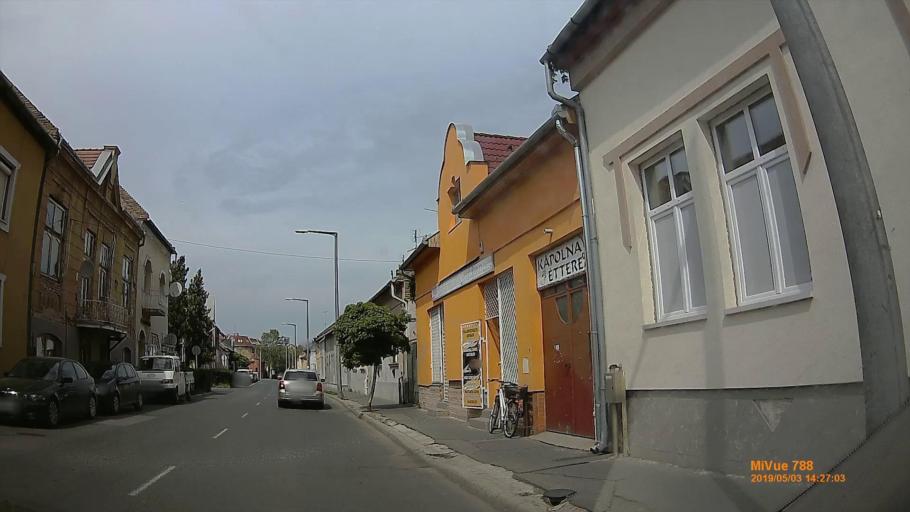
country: HU
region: Jasz-Nagykun-Szolnok
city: Szolnok
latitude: 47.1765
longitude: 20.1893
